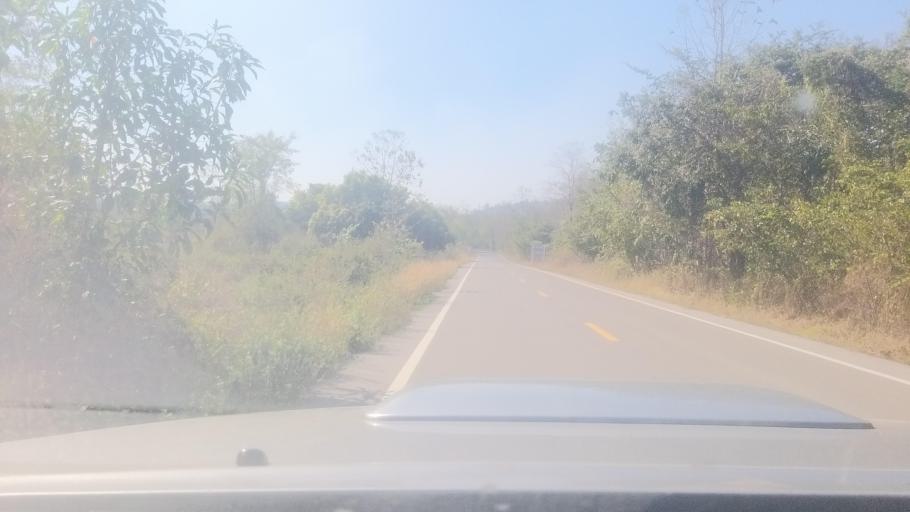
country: TH
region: Phrae
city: Nong Muang Khai
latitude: 18.2970
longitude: 100.0482
